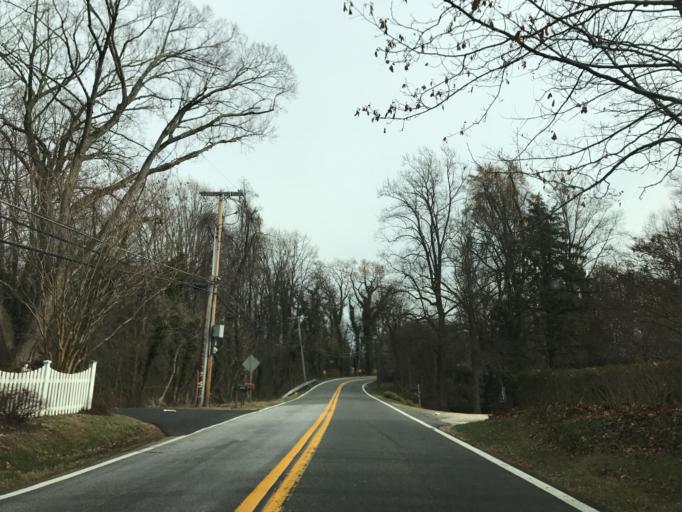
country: US
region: Maryland
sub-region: Anne Arundel County
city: Arnold
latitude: 39.0402
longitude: -76.5173
